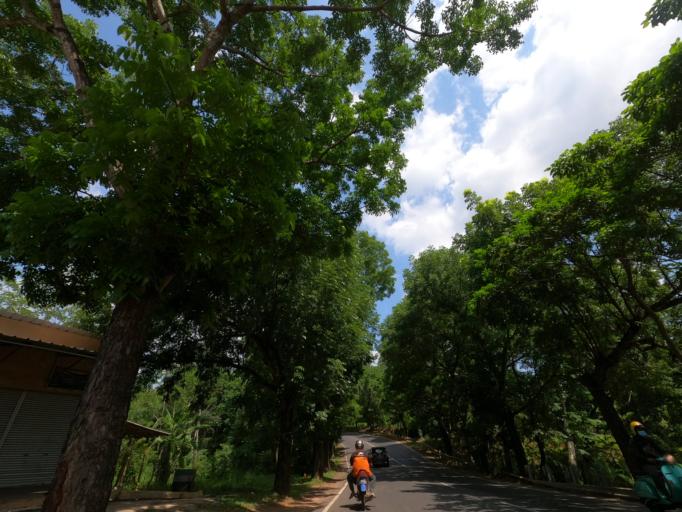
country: ID
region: West Java
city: Pamanukan
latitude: -6.5538
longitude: 107.7462
